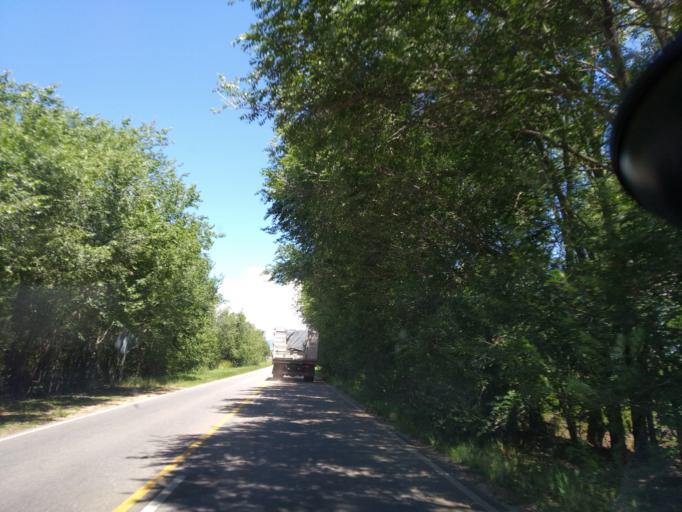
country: AR
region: Cordoba
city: Villa Cura Brochero
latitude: -31.6716
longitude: -65.0934
